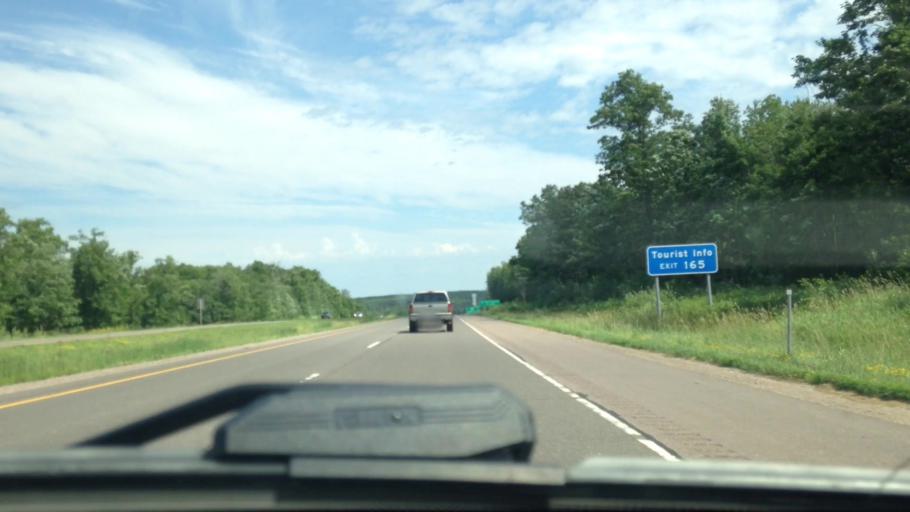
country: US
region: Wisconsin
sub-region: Washburn County
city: Spooner
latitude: 45.8088
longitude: -91.8565
